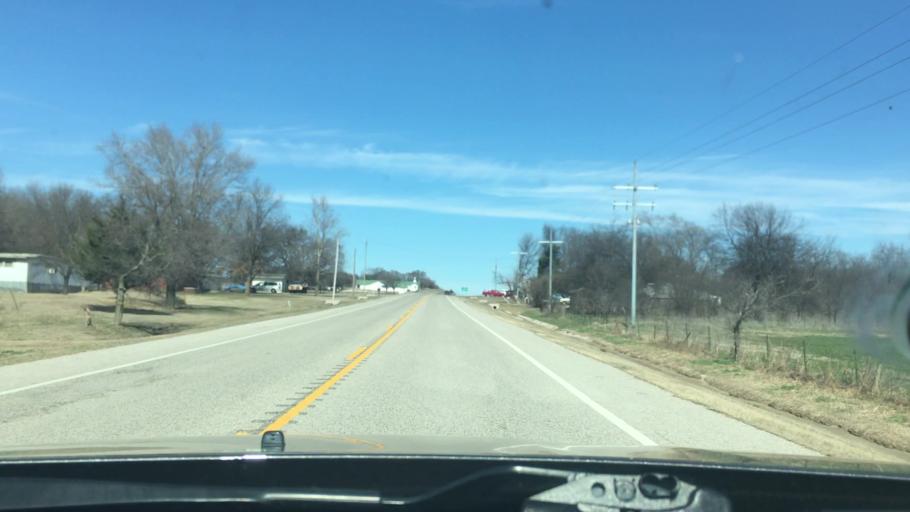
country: US
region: Oklahoma
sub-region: Murray County
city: Sulphur
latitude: 34.3997
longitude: -96.9510
